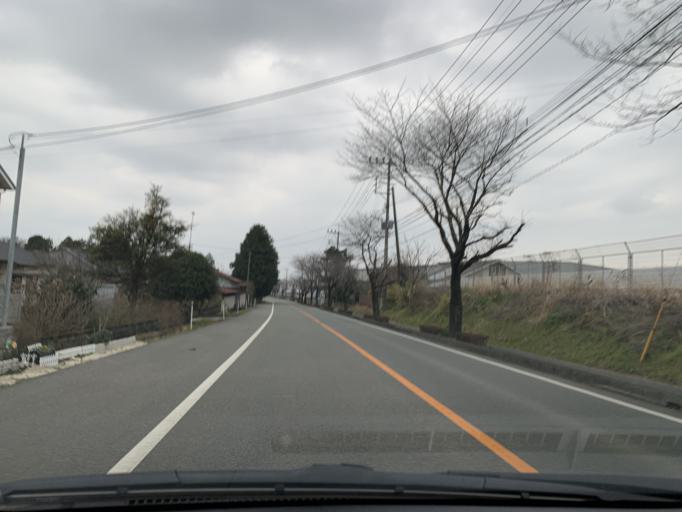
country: JP
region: Kumamoto
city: Ozu
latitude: 32.8903
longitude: 130.8936
